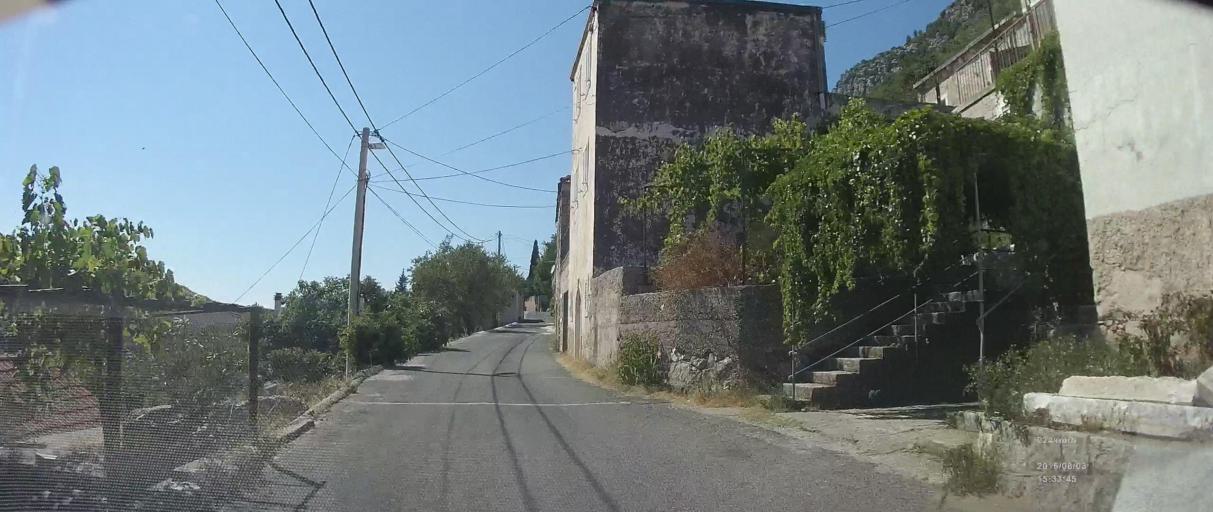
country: HR
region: Dubrovacko-Neretvanska
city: Blato
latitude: 42.7348
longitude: 17.5532
